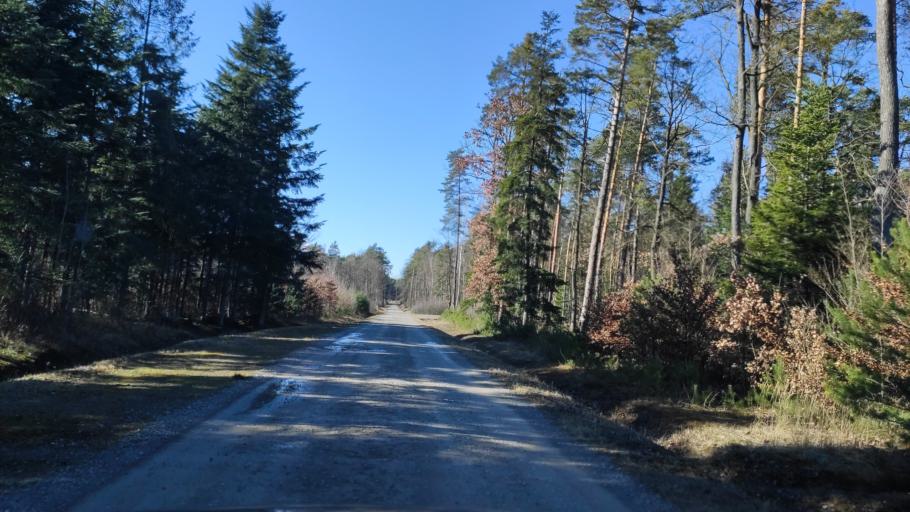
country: PL
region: Masovian Voivodeship
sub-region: Powiat radomski
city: Jedlnia-Letnisko
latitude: 51.4706
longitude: 21.3041
